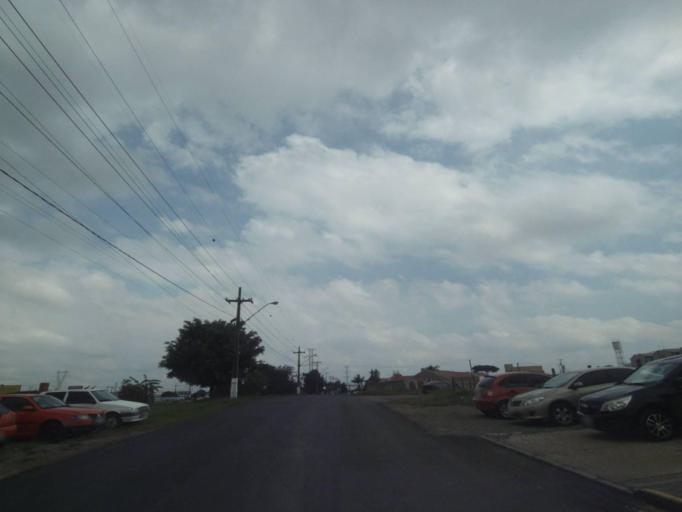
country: BR
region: Parana
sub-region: Curitiba
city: Curitiba
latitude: -25.4924
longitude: -49.3447
